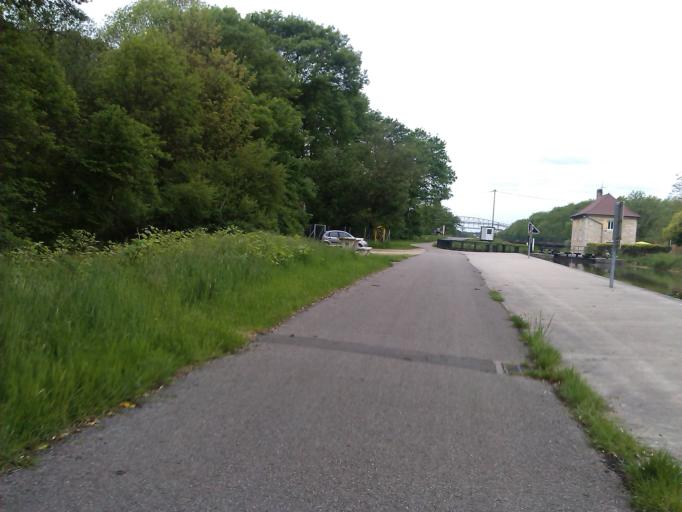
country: FR
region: Franche-Comte
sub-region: Departement du Jura
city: Damparis
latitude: 47.0595
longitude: 5.4146
